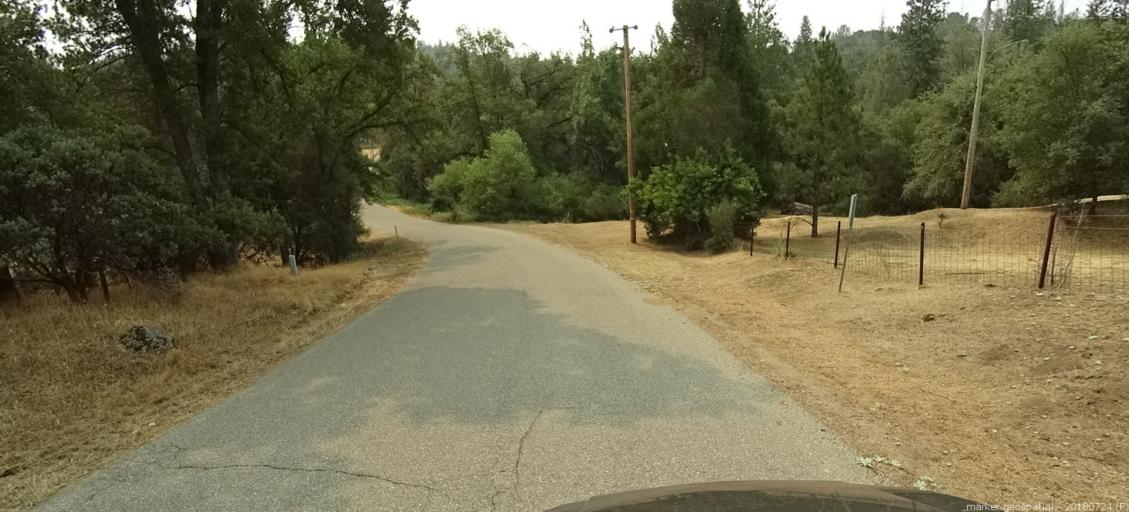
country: US
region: California
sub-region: Madera County
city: Oakhurst
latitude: 37.3326
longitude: -119.6113
